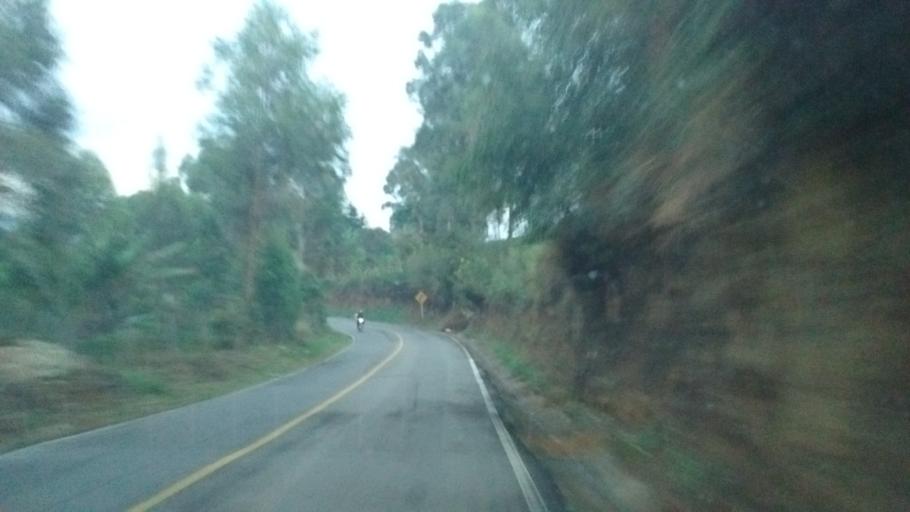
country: CO
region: Cauca
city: Popayan
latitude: 2.3671
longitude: -76.6870
